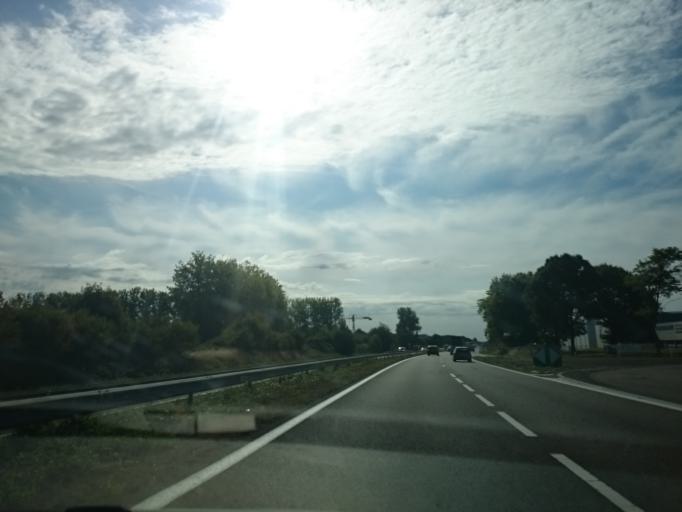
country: FR
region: Brittany
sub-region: Departement d'Ille-et-Vilaine
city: Bedee
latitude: 48.1818
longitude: -1.9323
